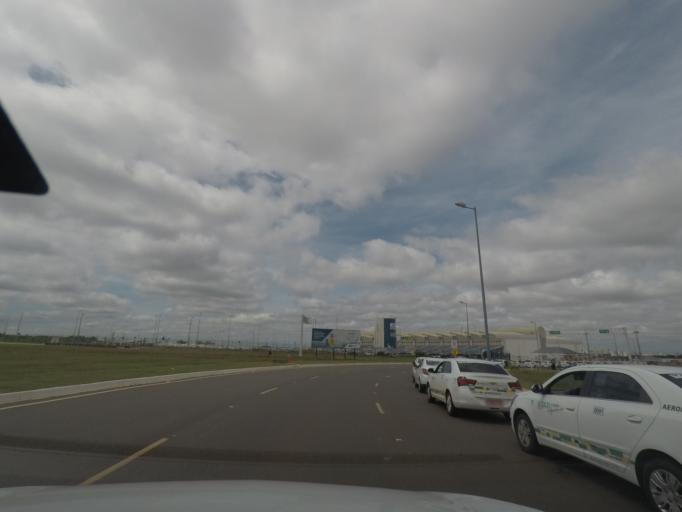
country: BR
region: Goias
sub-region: Goiania
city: Goiania
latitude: -16.6268
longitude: -49.2131
